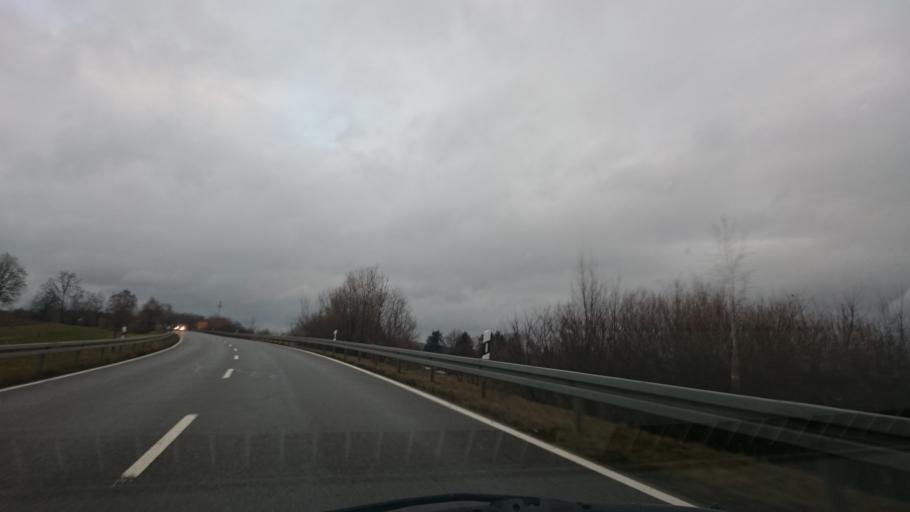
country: DE
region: Saxony
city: Lichtenstein
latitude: 50.7673
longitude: 12.6204
